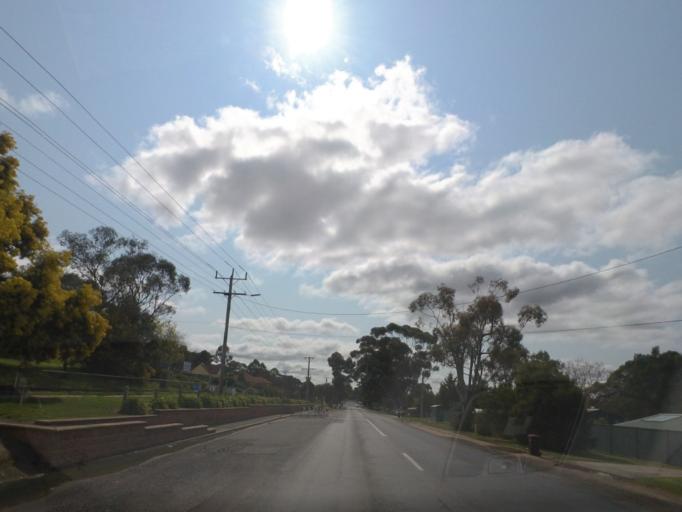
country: AU
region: Victoria
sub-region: Murrindindi
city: Kinglake West
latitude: -37.0973
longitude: 145.1014
